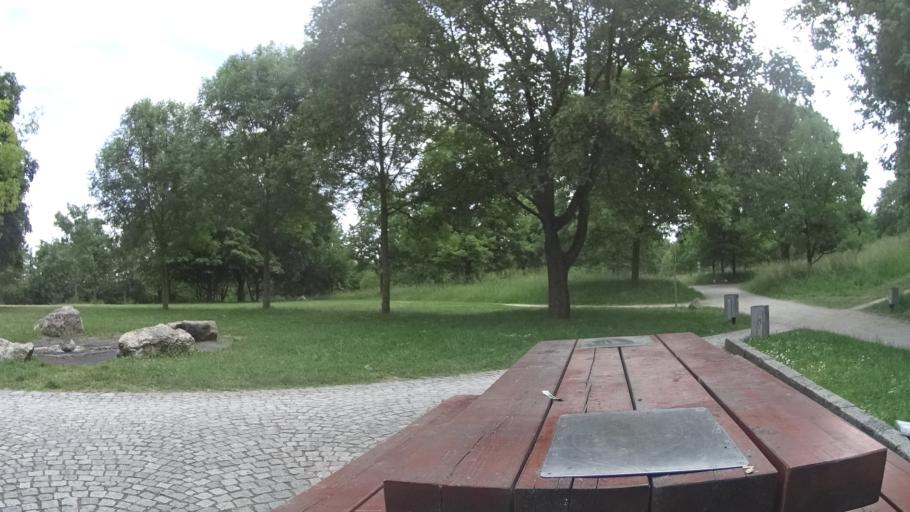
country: DE
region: Bavaria
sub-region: Upper Palatinate
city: Sinzing
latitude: 49.0237
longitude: 12.0454
